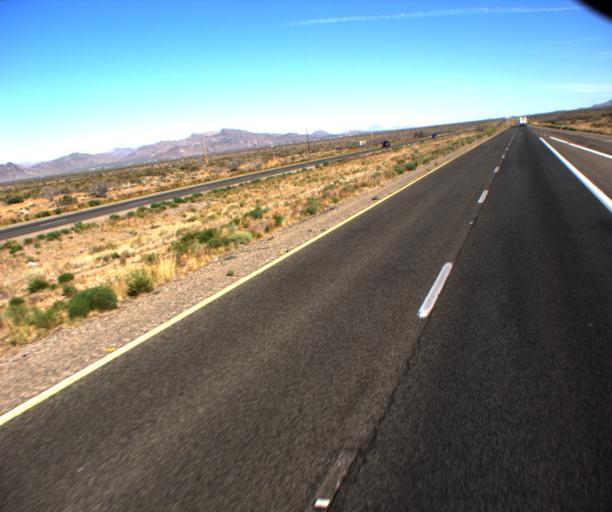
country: US
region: Arizona
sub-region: Mohave County
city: Golden Valley
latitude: 35.2990
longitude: -114.1883
